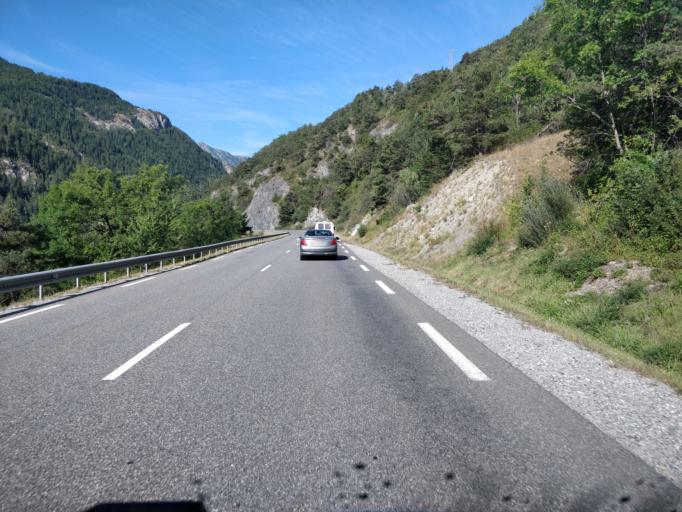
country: FR
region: Provence-Alpes-Cote d'Azur
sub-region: Departement des Alpes-de-Haute-Provence
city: Barcelonnette
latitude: 44.3998
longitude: 6.5406
